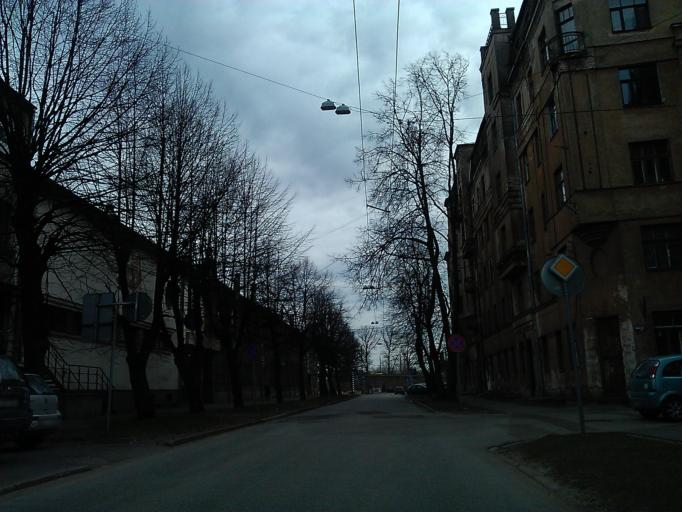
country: LV
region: Riga
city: Riga
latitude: 56.9703
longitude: 24.1513
